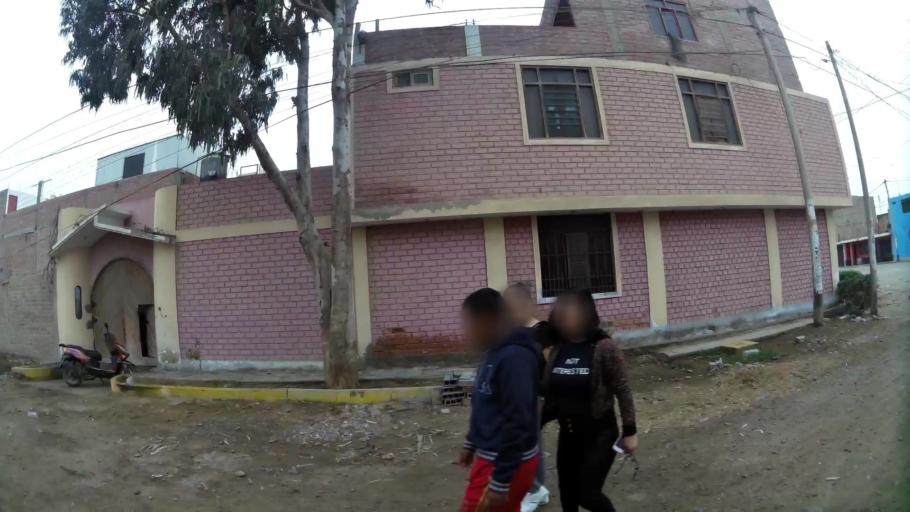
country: PE
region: Ica
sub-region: Provincia de Pisco
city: Pisco
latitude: -13.7191
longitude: -76.2138
